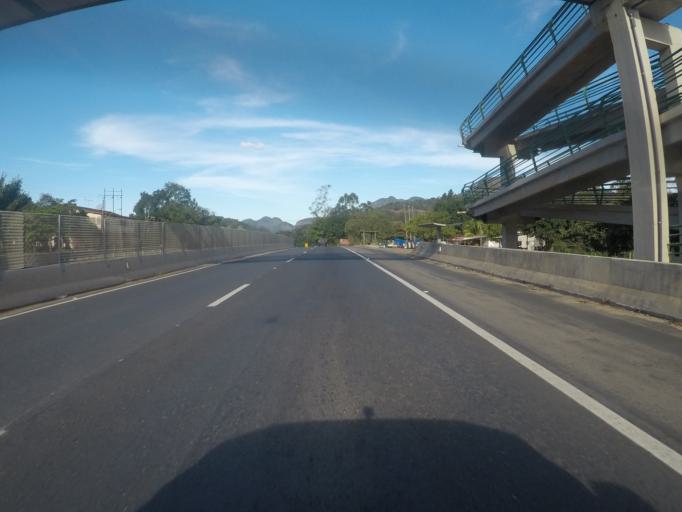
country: BR
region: Espirito Santo
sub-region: Ibiracu
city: Ibiracu
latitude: -19.8645
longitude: -40.3897
